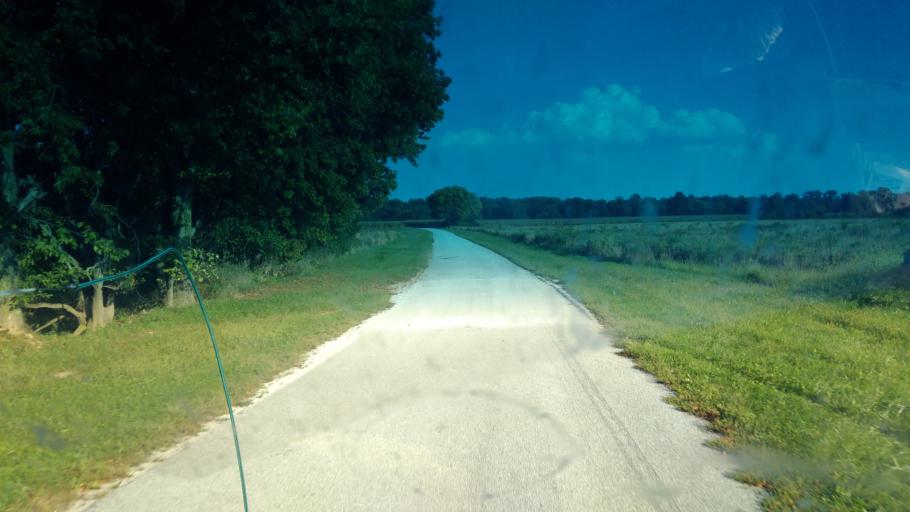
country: US
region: Ohio
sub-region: Wyandot County
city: Upper Sandusky
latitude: 40.9291
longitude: -83.2543
